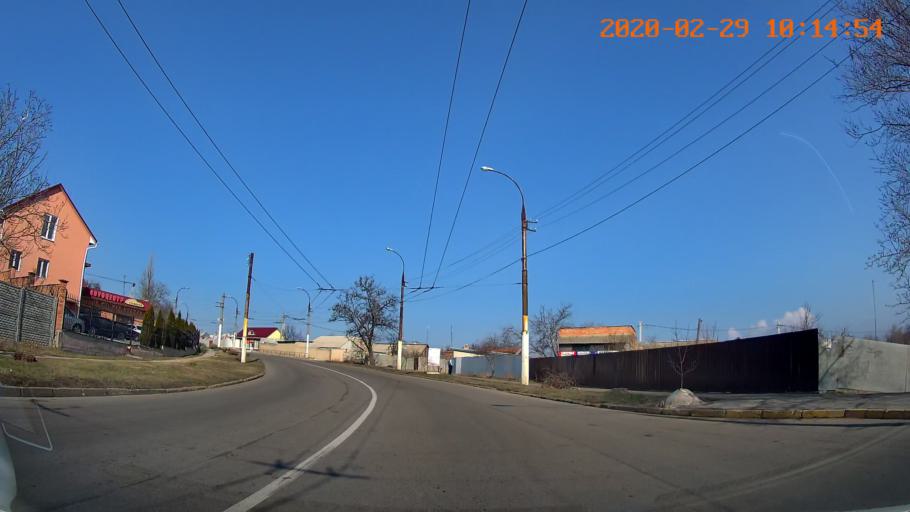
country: MD
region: Telenesti
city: Tiraspolul Nou
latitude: 46.8512
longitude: 29.6430
